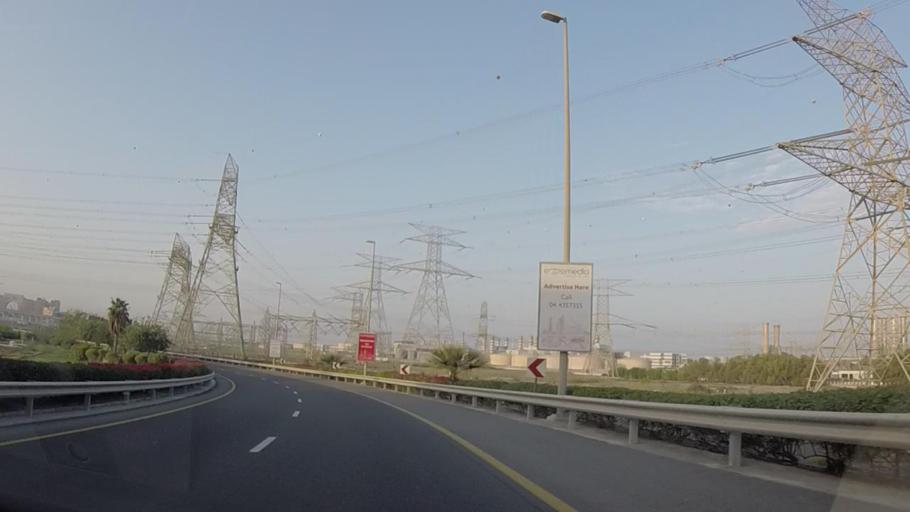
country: AE
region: Dubai
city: Dubai
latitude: 25.0544
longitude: 55.1219
